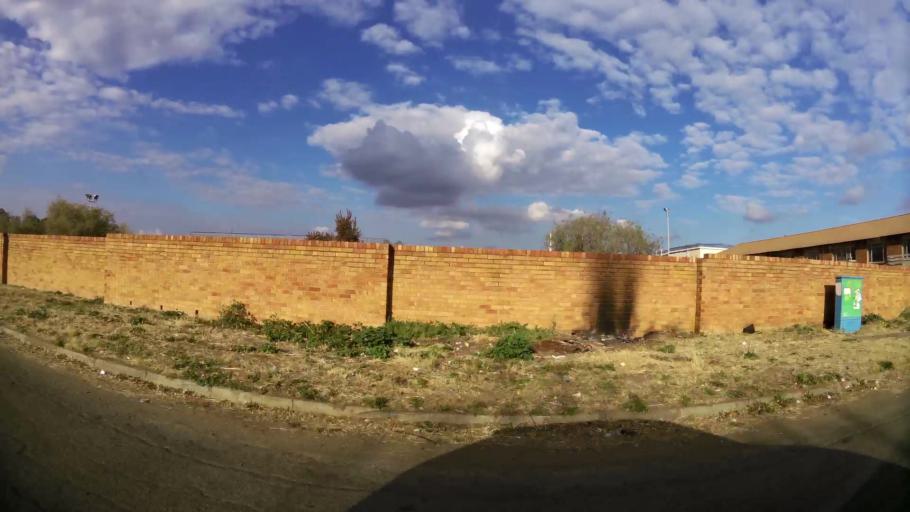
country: ZA
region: Orange Free State
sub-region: Mangaung Metropolitan Municipality
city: Bloemfontein
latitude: -29.1069
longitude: 26.1977
